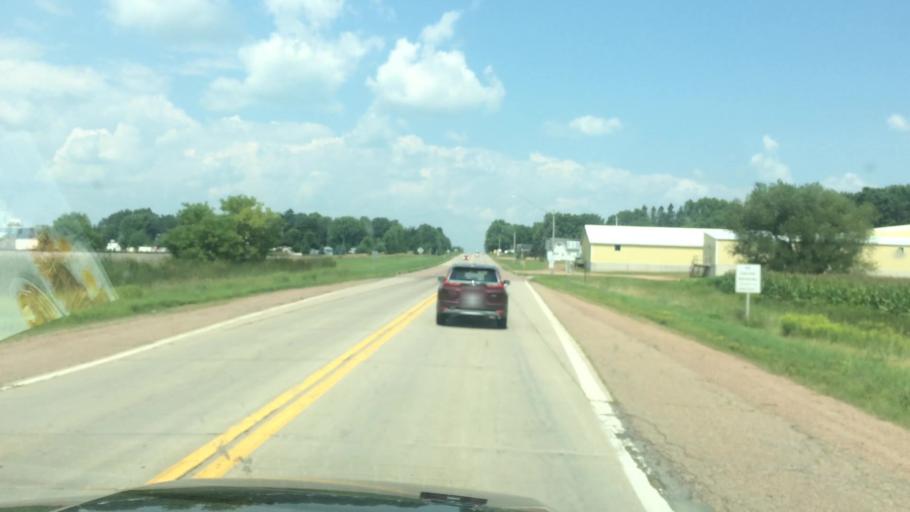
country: US
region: Wisconsin
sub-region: Clark County
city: Colby
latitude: 44.8432
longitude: -90.3159
